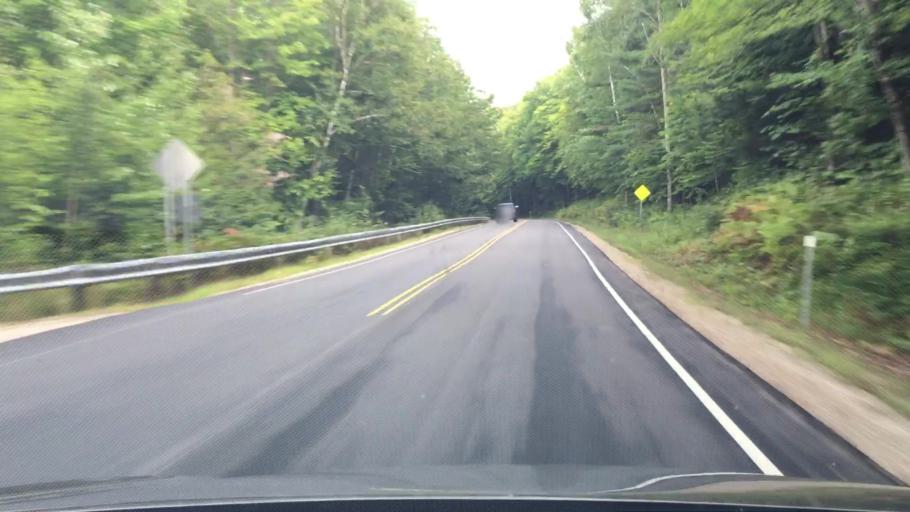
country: US
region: New Hampshire
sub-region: Carroll County
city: Conway
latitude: 43.9905
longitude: -71.1790
